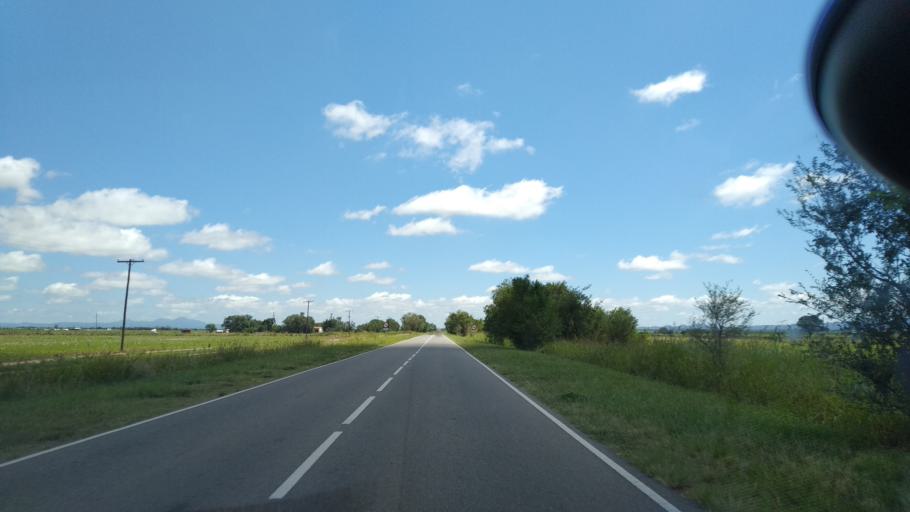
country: AR
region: Cordoba
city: Villa Cura Brochero
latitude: -31.5875
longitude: -65.1114
